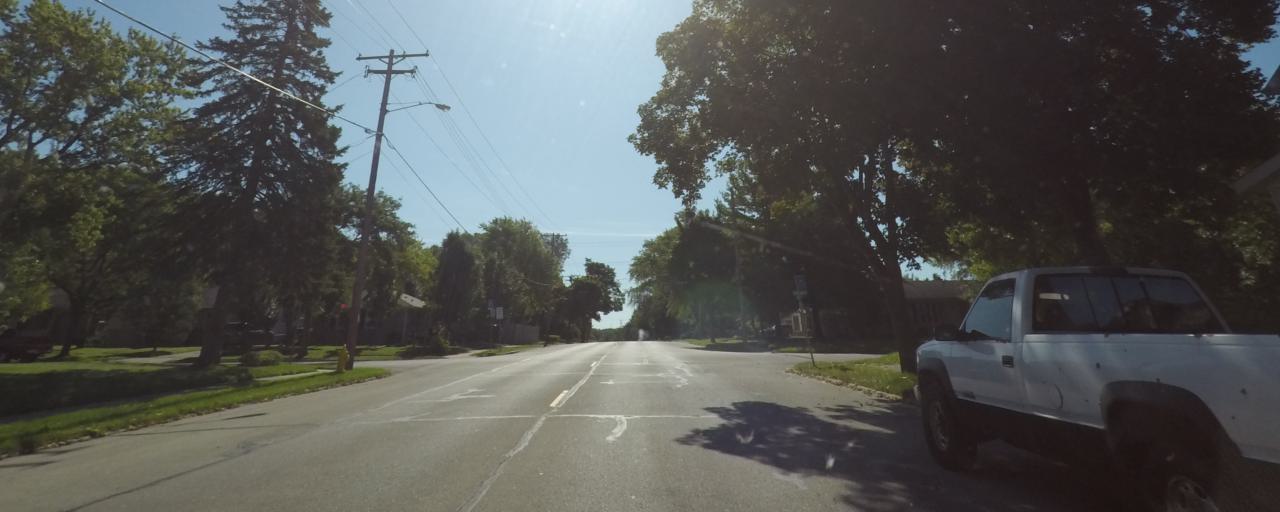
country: US
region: Wisconsin
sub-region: Waukesha County
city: Waukesha
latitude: 43.0006
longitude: -88.2135
